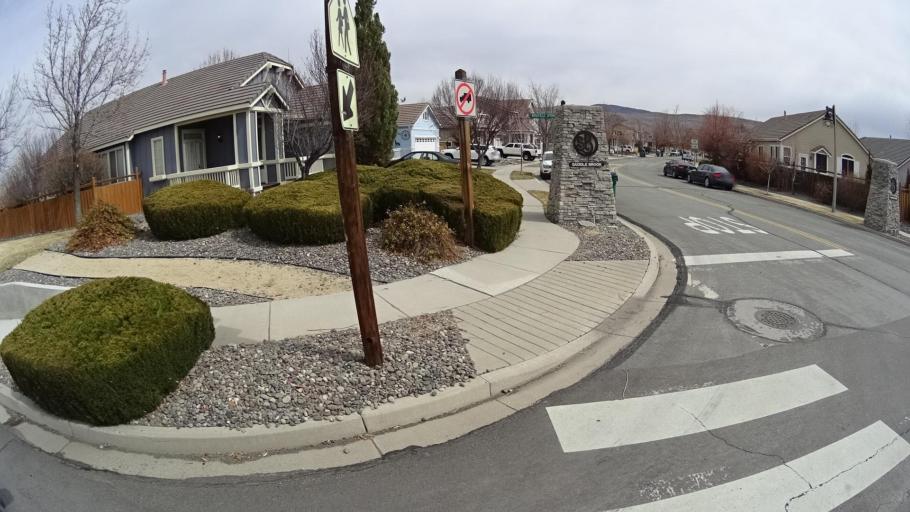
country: US
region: Nevada
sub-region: Washoe County
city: Spanish Springs
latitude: 39.6247
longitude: -119.6860
